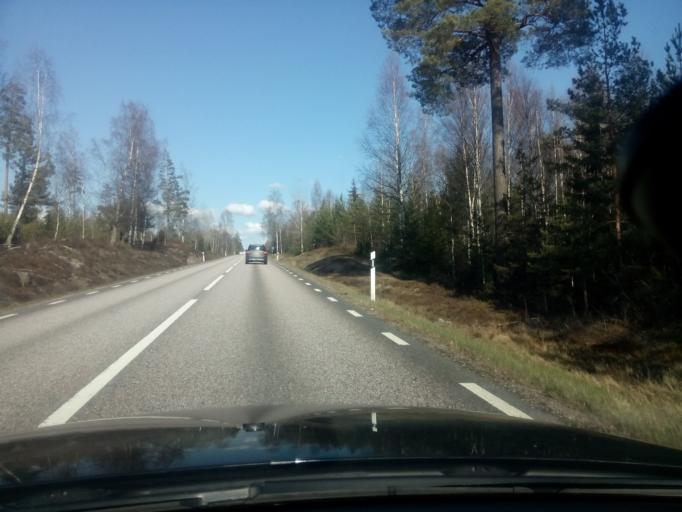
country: SE
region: Soedermanland
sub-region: Flens Kommun
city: Malmkoping
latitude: 59.2056
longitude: 16.8326
